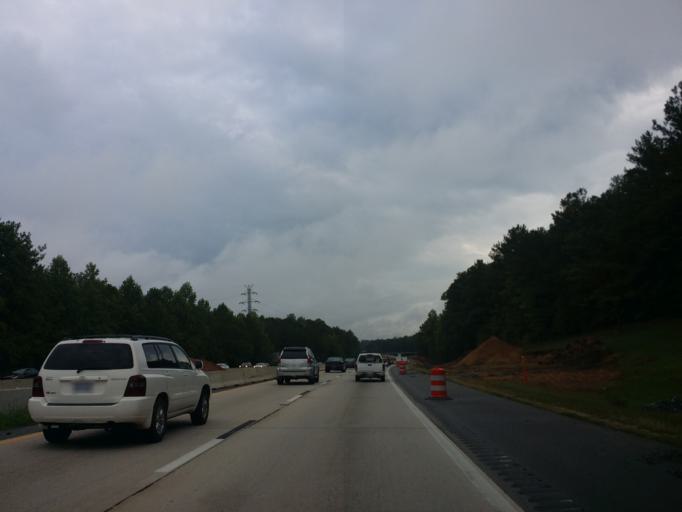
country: US
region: North Carolina
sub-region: Durham County
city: Durham
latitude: 35.9510
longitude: -78.8640
